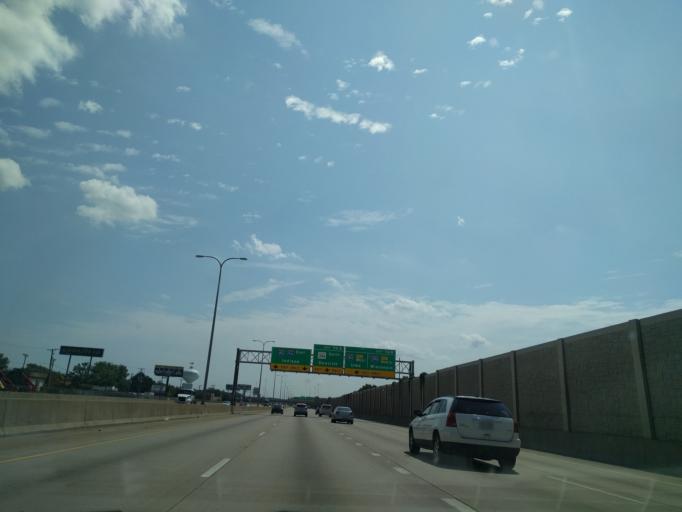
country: US
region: Illinois
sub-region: Cook County
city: South Holland
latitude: 41.5935
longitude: -87.5837
